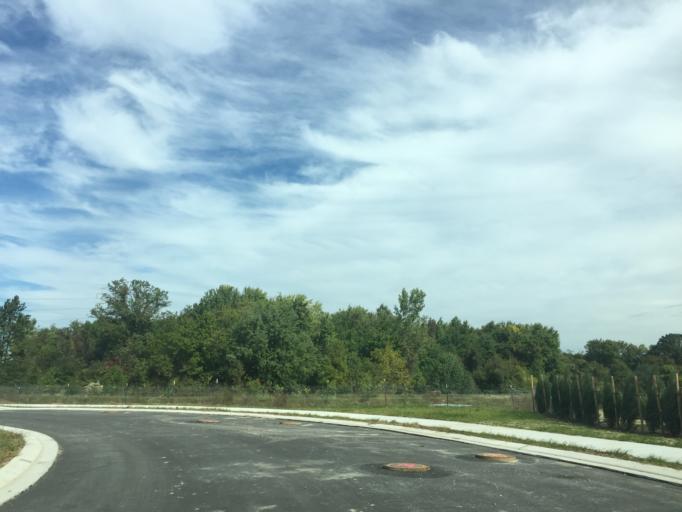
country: US
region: Maryland
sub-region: Baltimore County
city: Middle River
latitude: 39.3513
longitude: -76.4469
